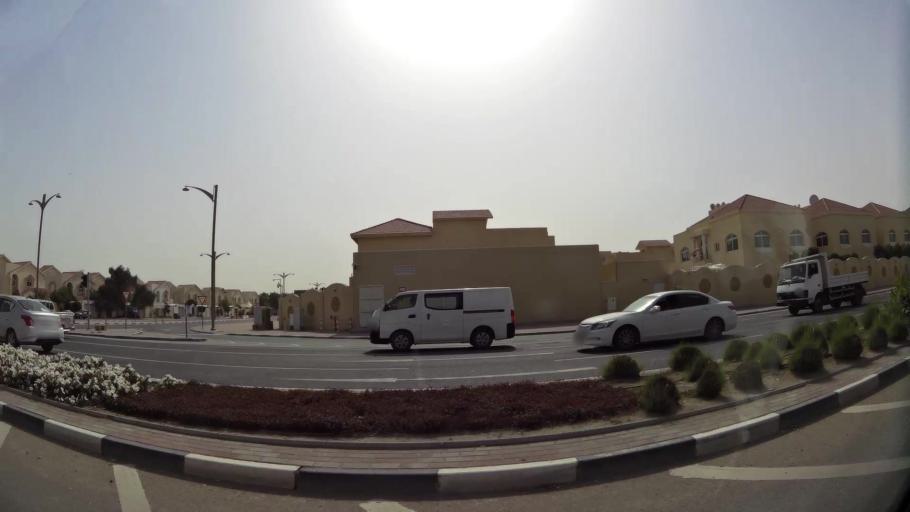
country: QA
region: Baladiyat ad Dawhah
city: Doha
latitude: 25.2618
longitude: 51.4805
